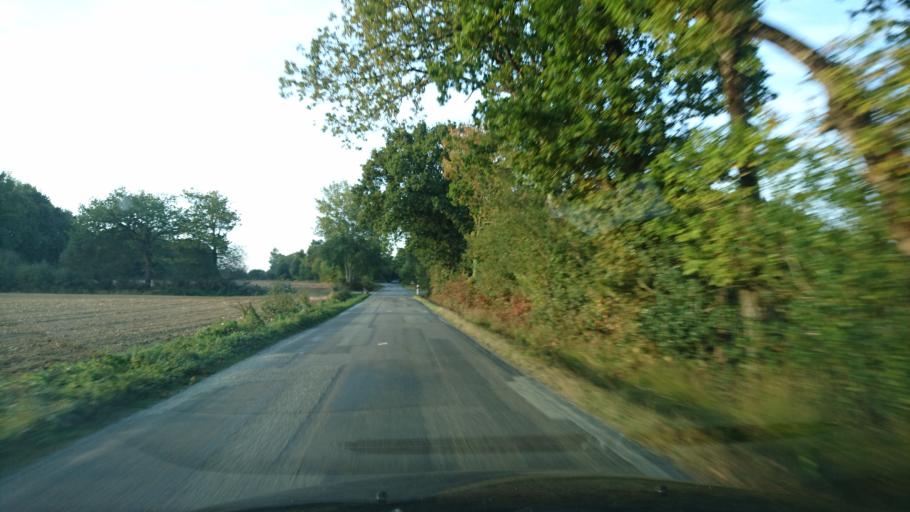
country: FR
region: Brittany
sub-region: Departement d'Ille-et-Vilaine
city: Bains-sur-Oust
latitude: 47.7420
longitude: -2.0516
